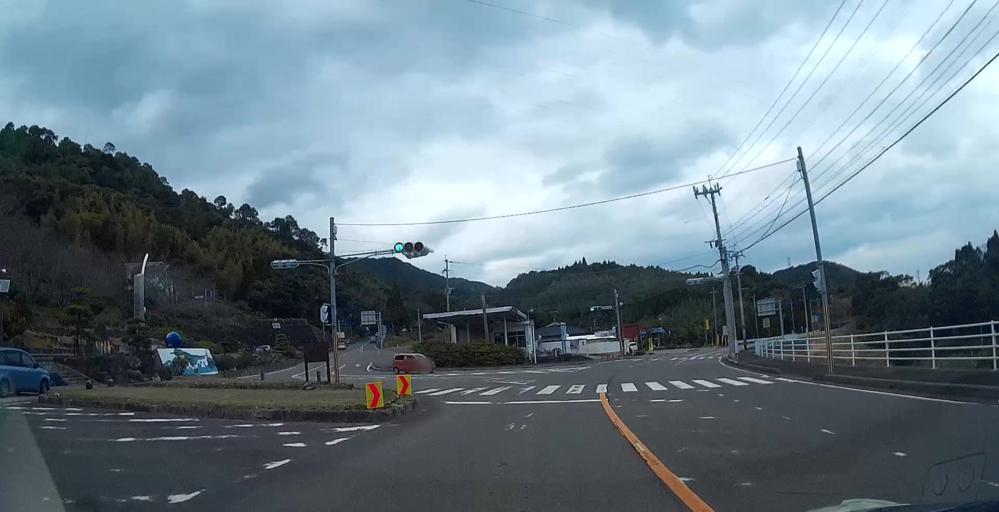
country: JP
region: Kagoshima
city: Akune
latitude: 32.1076
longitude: 130.1663
